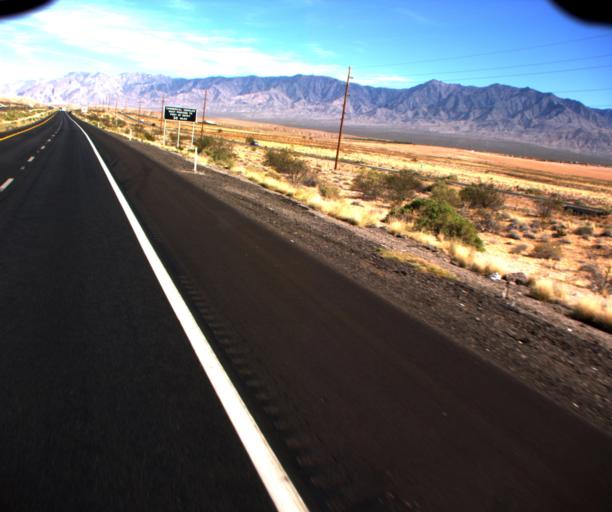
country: US
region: Nevada
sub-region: Clark County
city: Mesquite
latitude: 36.8217
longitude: -114.0343
